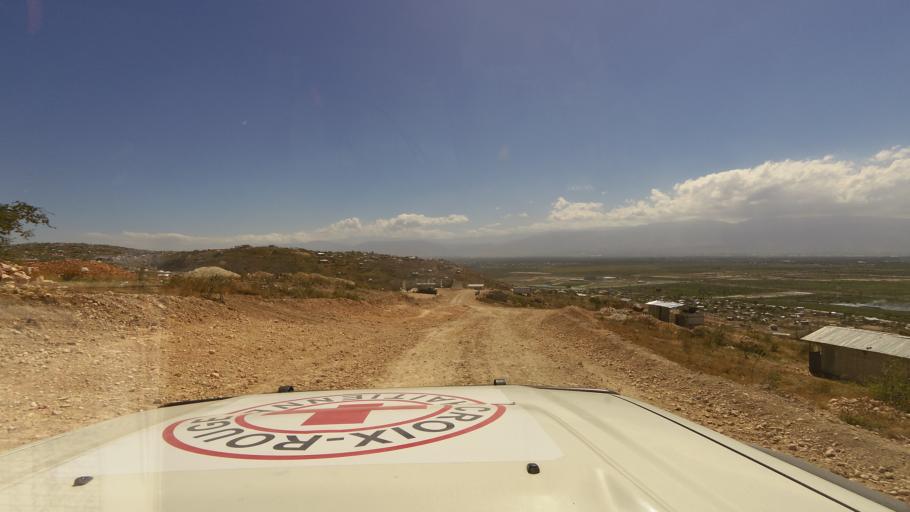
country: HT
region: Ouest
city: Croix des Bouquets
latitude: 18.6698
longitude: -72.2942
